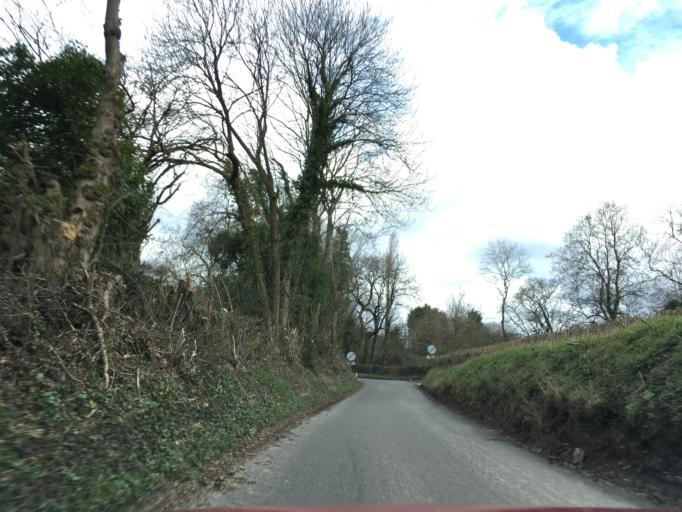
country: GB
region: England
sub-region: Gloucestershire
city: Coleford
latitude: 51.7553
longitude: -2.6337
